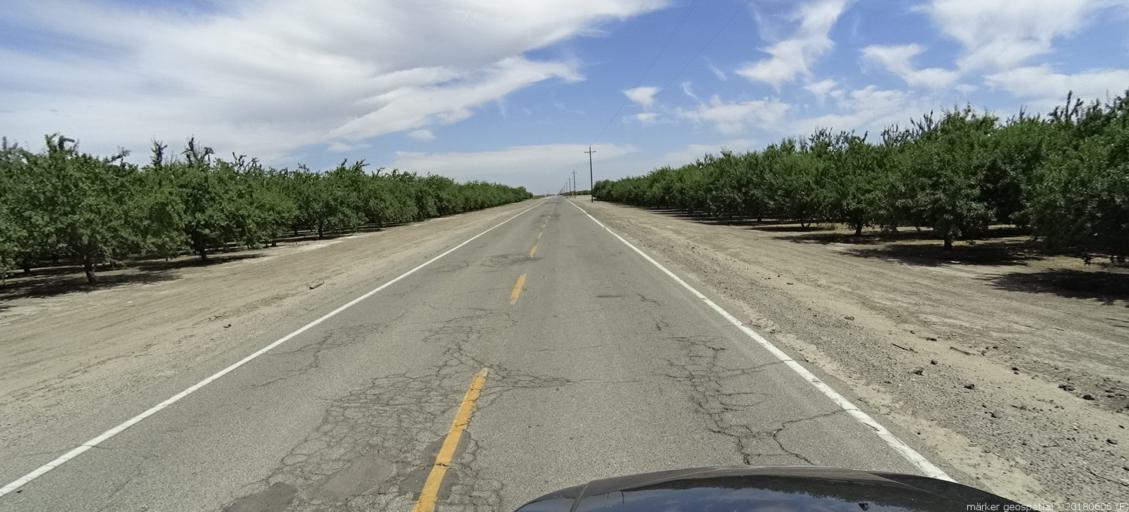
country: US
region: California
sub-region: Fresno County
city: Firebaugh
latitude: 36.8640
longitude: -120.3818
